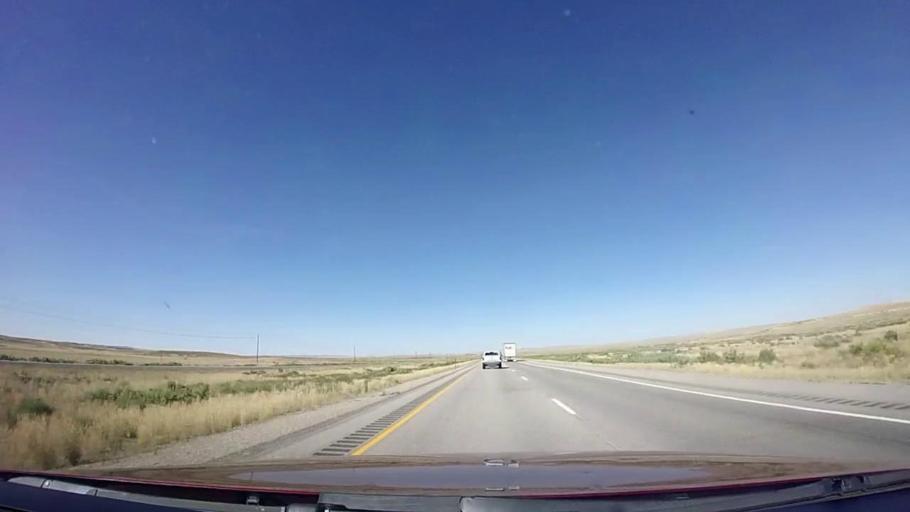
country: US
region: Wyoming
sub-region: Carbon County
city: Rawlins
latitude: 41.7821
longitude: -107.4260
